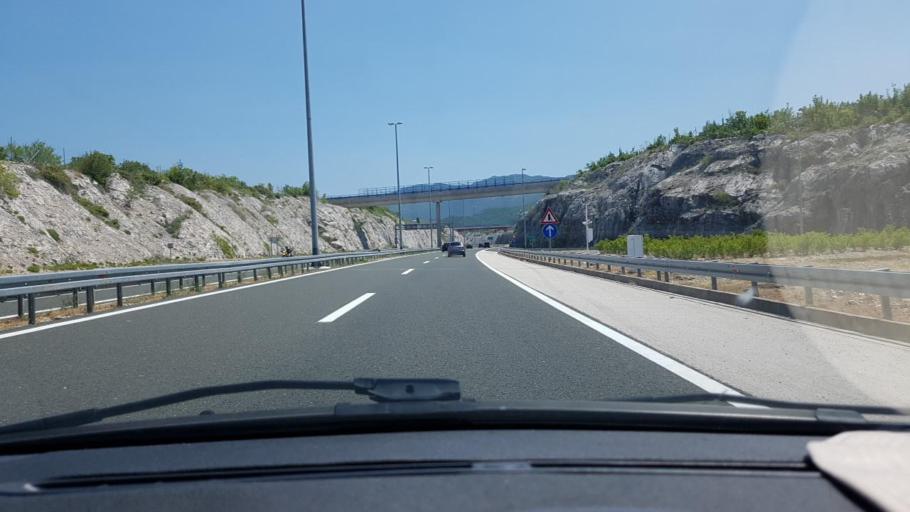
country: HR
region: Splitsko-Dalmatinska
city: Vrgorac
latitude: 43.2186
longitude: 17.2633
